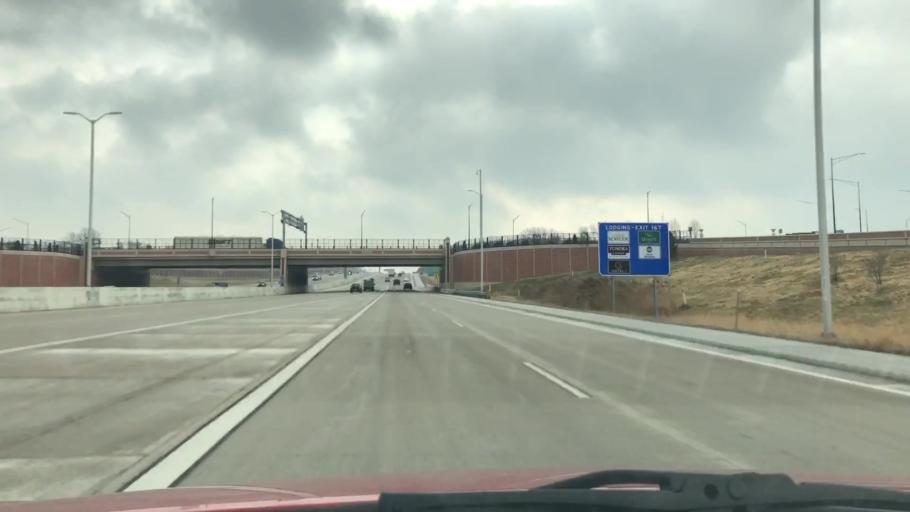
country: US
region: Wisconsin
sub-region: Brown County
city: Howard
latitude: 44.5256
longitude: -88.0822
